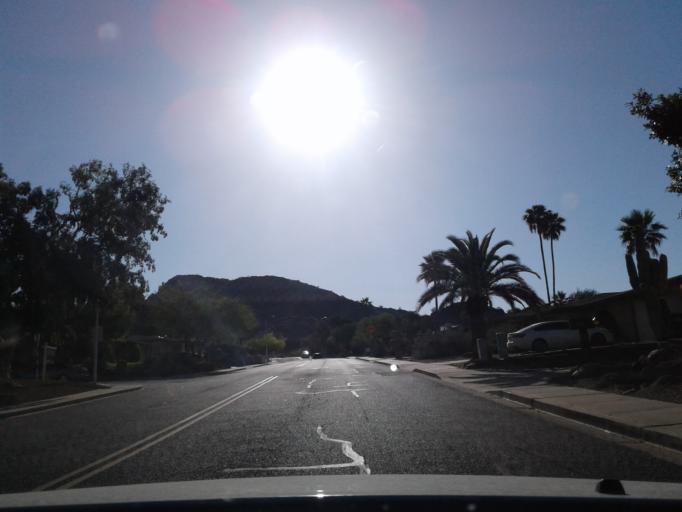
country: US
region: Arizona
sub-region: Maricopa County
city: Paradise Valley
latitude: 33.5367
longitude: -112.0303
